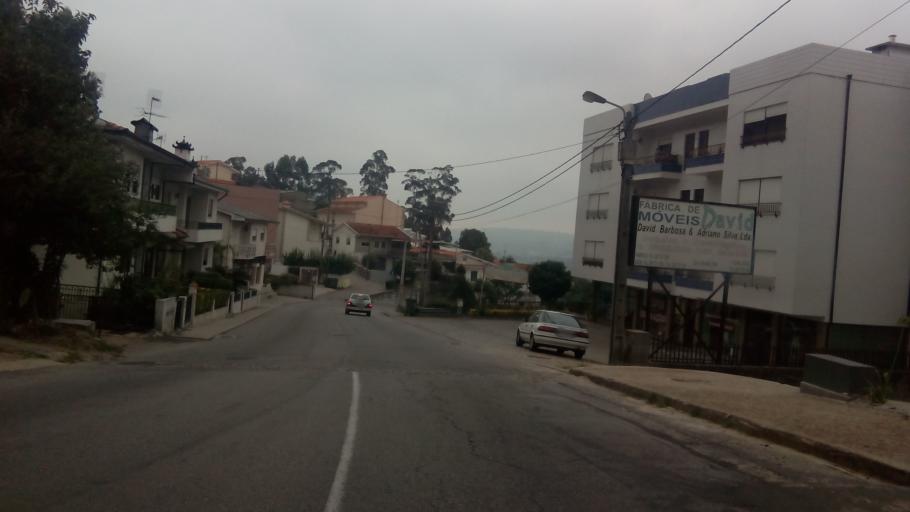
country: PT
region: Porto
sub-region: Paredes
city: Madalena
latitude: 41.2163
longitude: -8.3550
